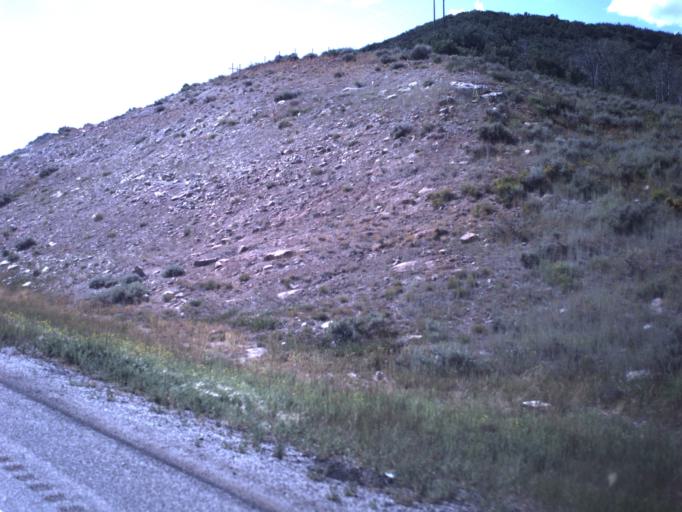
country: US
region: Utah
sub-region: Summit County
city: Francis
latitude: 40.2005
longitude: -110.9904
